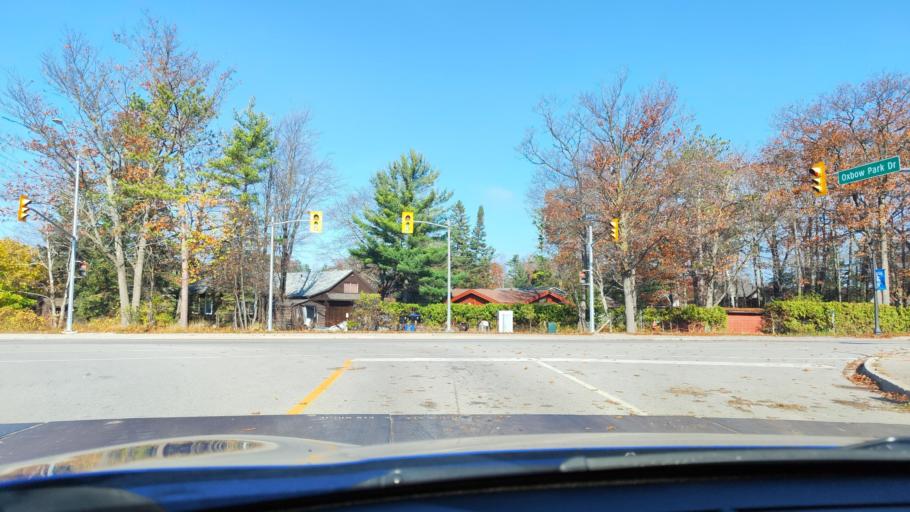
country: CA
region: Ontario
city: Wasaga Beach
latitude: 44.4904
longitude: -80.0472
